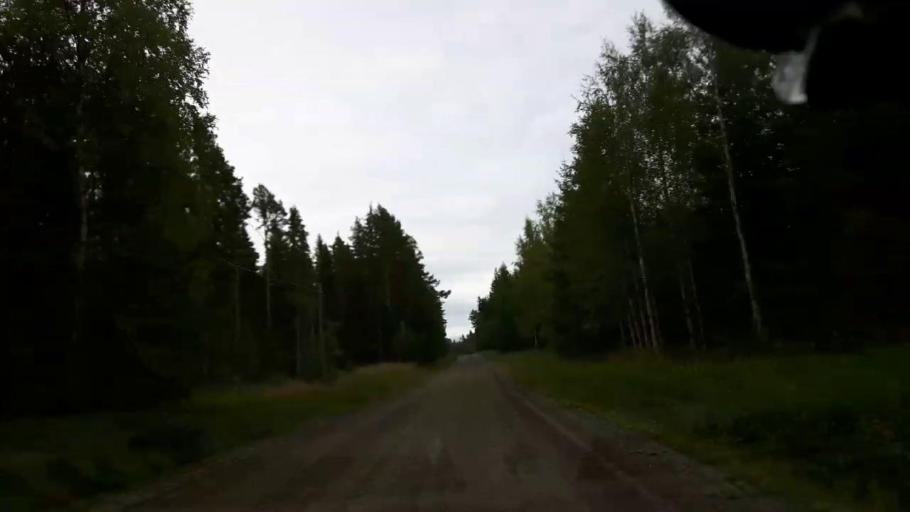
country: SE
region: Jaemtland
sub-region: Braecke Kommun
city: Braecke
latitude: 62.9203
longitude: 15.5571
